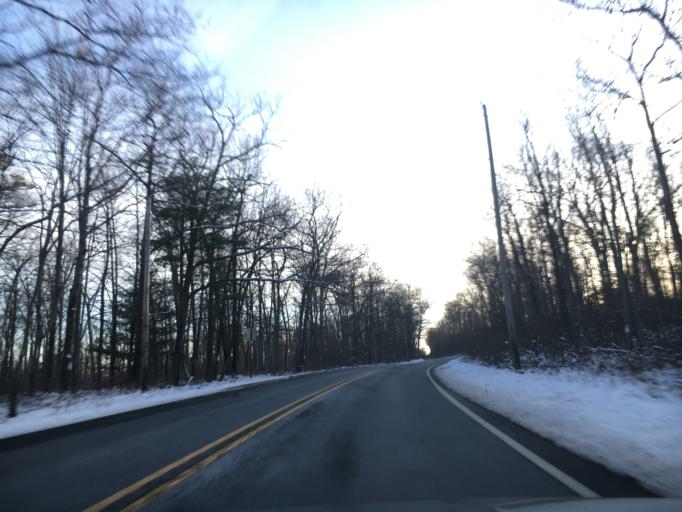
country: US
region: Pennsylvania
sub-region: Pike County
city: Hemlock Farms
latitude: 41.3546
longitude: -75.1289
